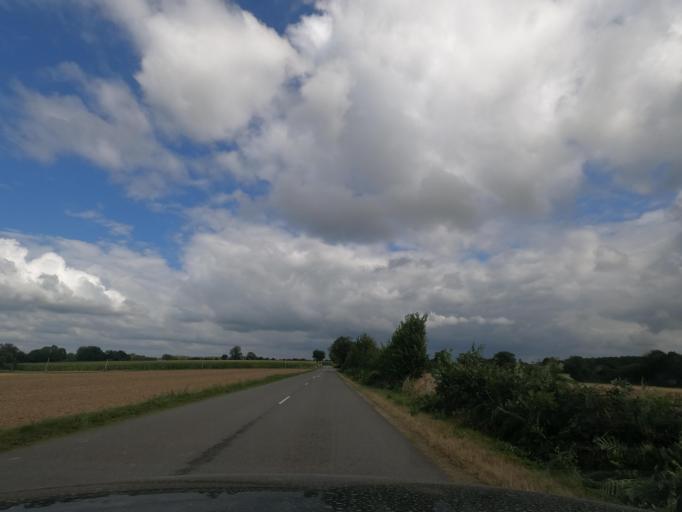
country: FR
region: Lower Normandy
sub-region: Departement de l'Orne
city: La Ferriere-aux-Etangs
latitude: 48.6880
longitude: -0.4740
